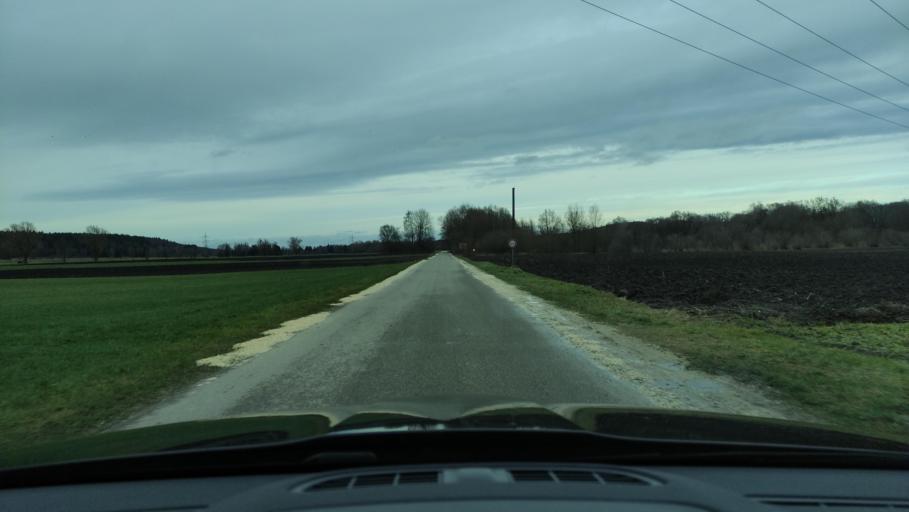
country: DE
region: Bavaria
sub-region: Swabia
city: Breitenthal
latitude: 48.2362
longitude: 10.3098
